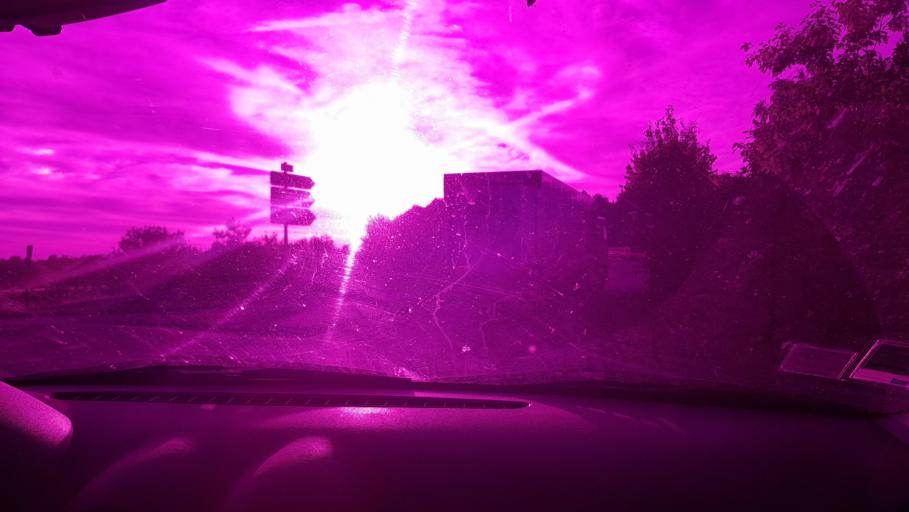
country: FR
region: Brittany
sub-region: Departement d'Ille-et-Vilaine
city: Erbree
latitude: 48.0879
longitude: -1.1051
